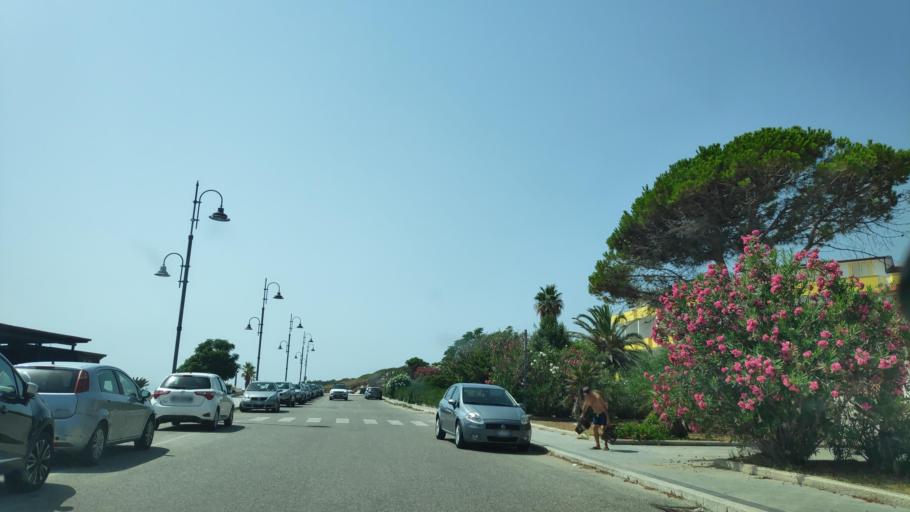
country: IT
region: Calabria
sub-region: Provincia di Catanzaro
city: Guardavalle Marina
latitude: 38.4797
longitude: 16.5801
